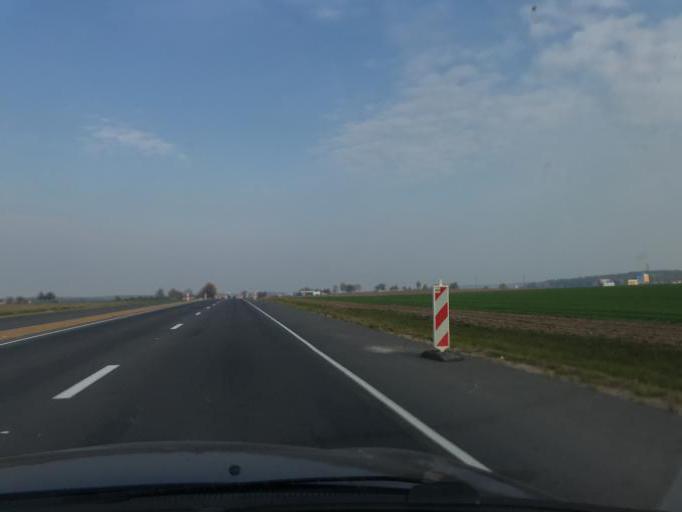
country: BY
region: Grodnenskaya
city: Shchuchin
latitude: 53.7220
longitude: 24.9657
